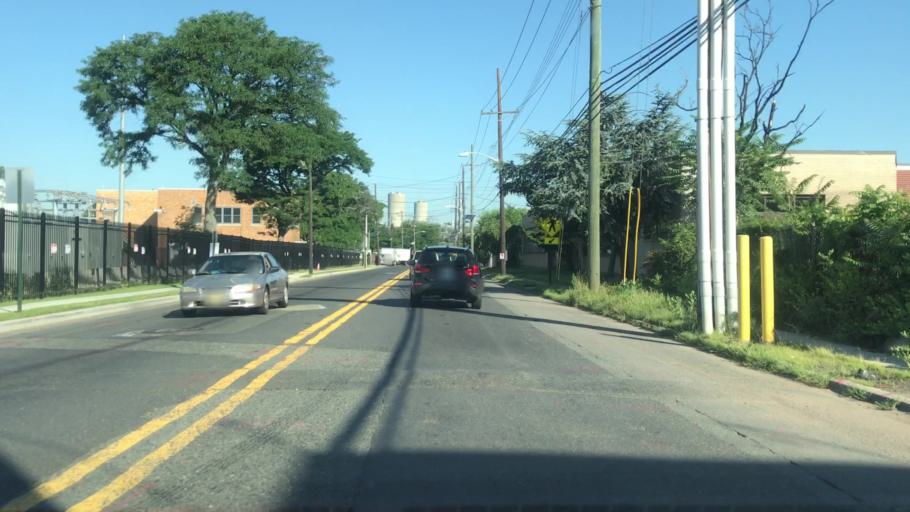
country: US
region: New Jersey
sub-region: Bergen County
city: Ridgefield
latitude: 40.8348
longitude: -74.0158
